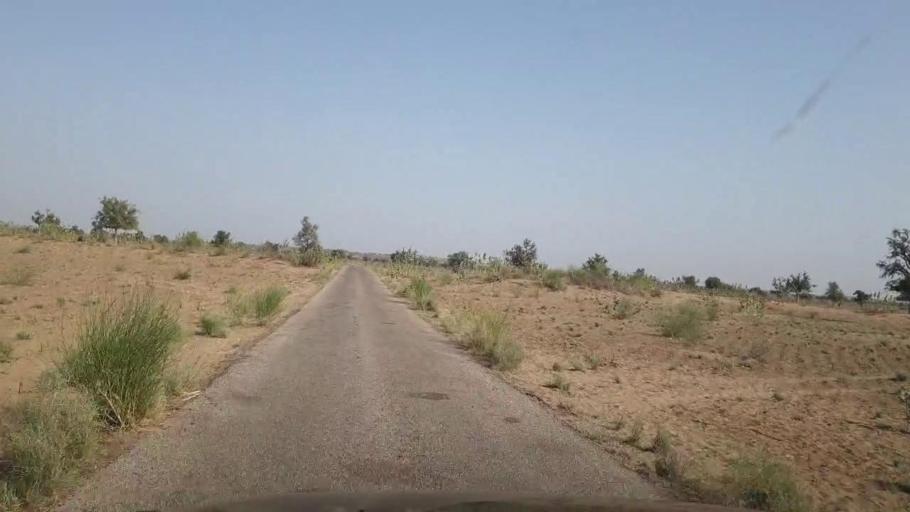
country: PK
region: Sindh
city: Islamkot
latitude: 25.1334
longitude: 70.4713
